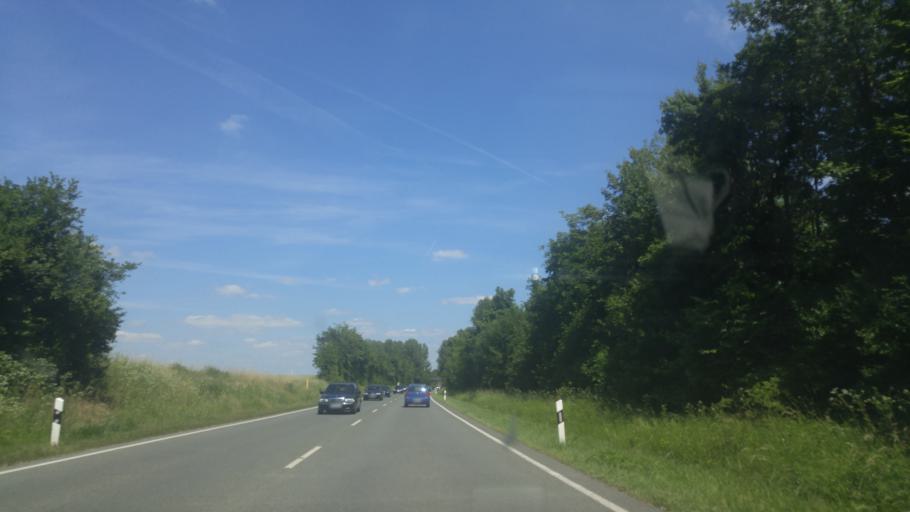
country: DE
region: Bavaria
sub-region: Regierungsbezirk Mittelfranken
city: Erlangen
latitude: 49.5714
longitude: 10.9529
